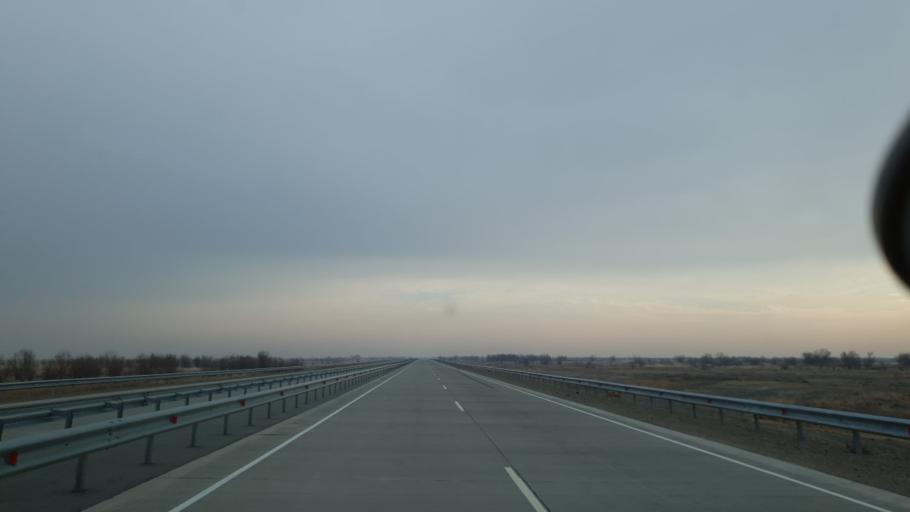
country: KZ
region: Almaty Oblysy
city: Zharkent
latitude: 44.0161
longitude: 79.7603
